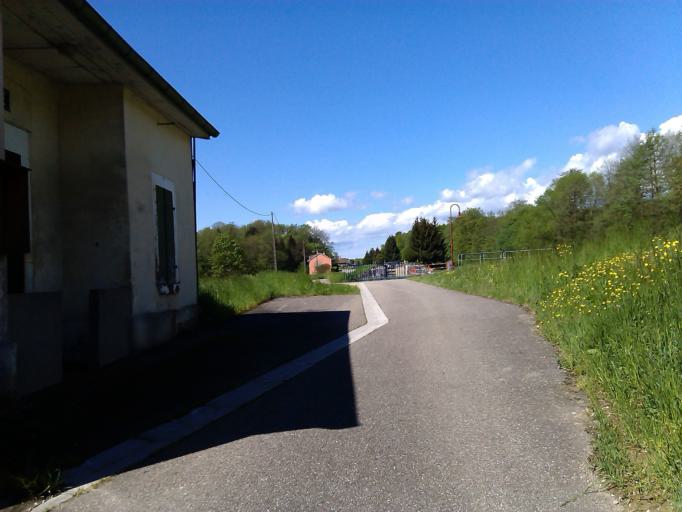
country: FR
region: Alsace
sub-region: Departement du Haut-Rhin
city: Dannemarie
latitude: 47.6340
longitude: 7.0725
